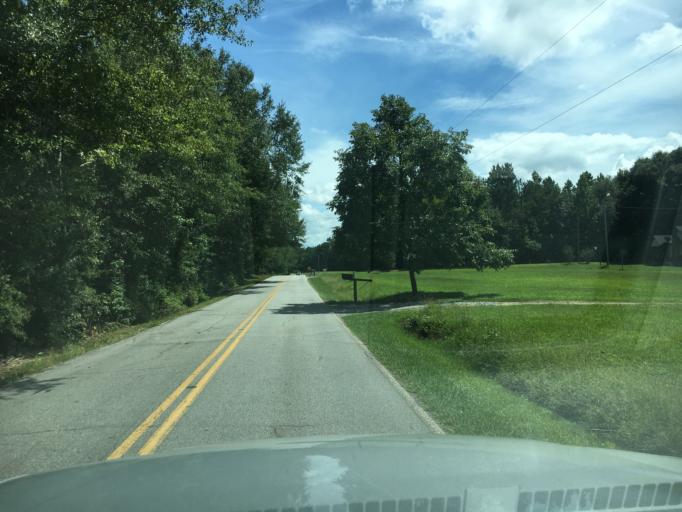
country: US
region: South Carolina
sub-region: Anderson County
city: Honea Path
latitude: 34.4964
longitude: -82.4038
